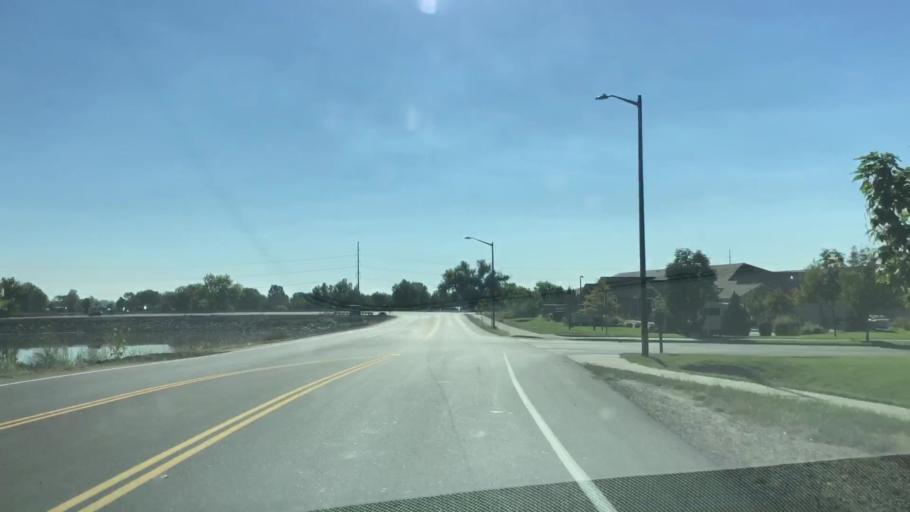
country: US
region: Colorado
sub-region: Larimer County
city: Loveland
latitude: 40.4289
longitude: -105.0490
